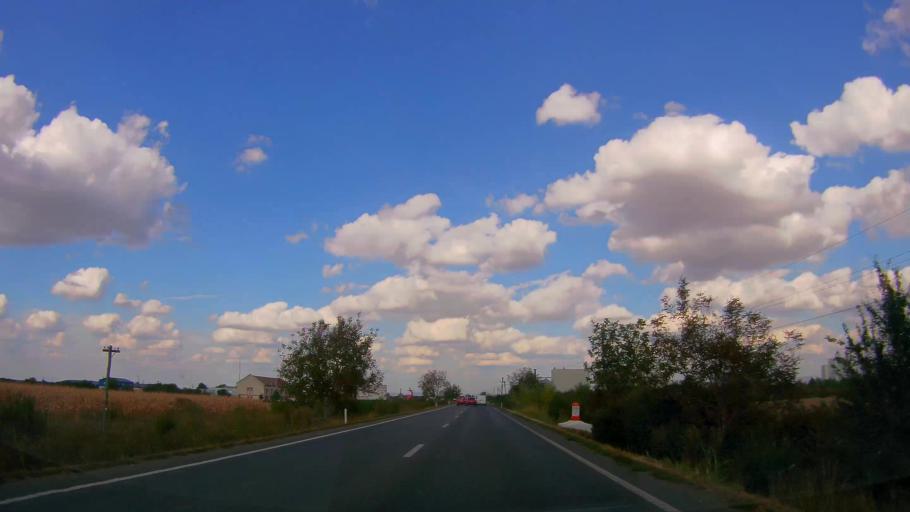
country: RO
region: Satu Mare
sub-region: Comuna Botiz
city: Botiz
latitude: 47.8180
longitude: 22.9334
